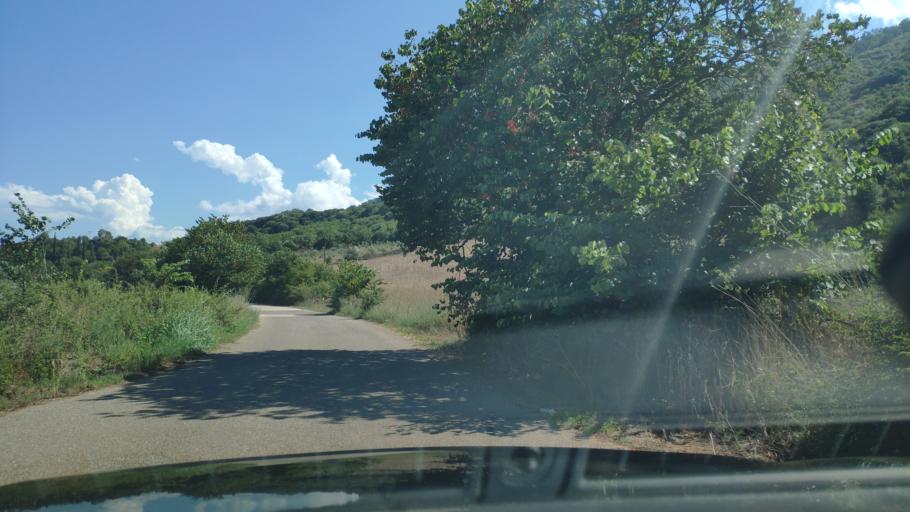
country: GR
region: West Greece
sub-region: Nomos Aitolias kai Akarnanias
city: Katouna
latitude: 38.8402
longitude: 21.0957
